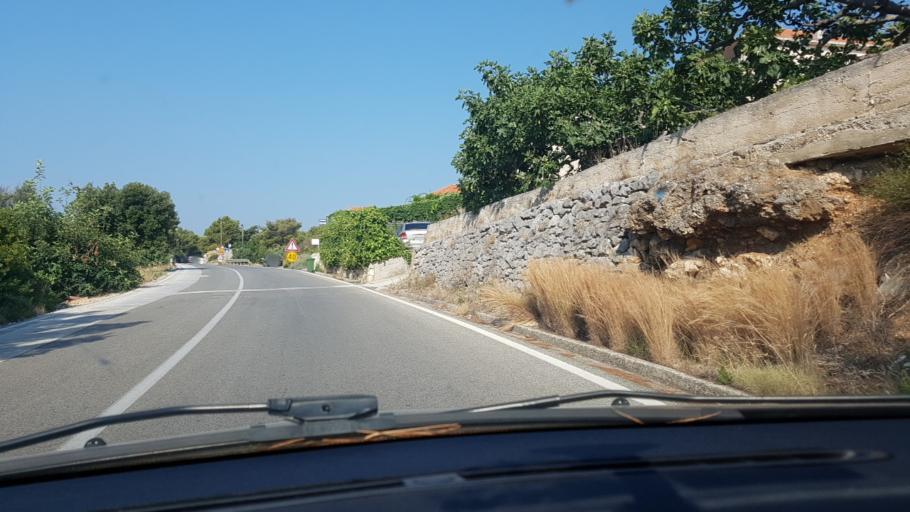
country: HR
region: Splitsko-Dalmatinska
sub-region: Grad Trogir
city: Trogir
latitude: 43.5150
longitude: 16.2071
